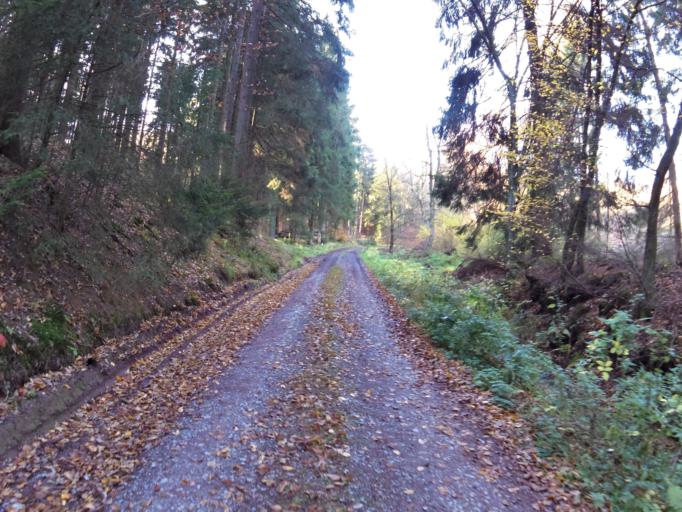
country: DE
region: Thuringia
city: Ruhla
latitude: 50.9015
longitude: 10.3466
